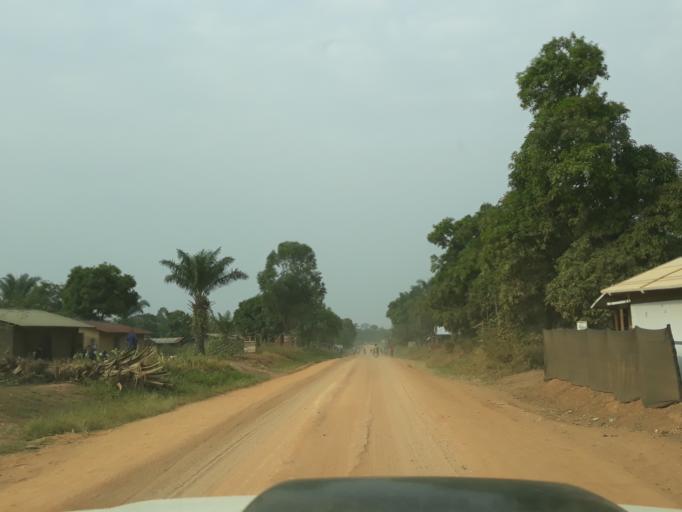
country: CD
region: Eastern Province
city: Bunia
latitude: 1.3515
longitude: 29.7602
